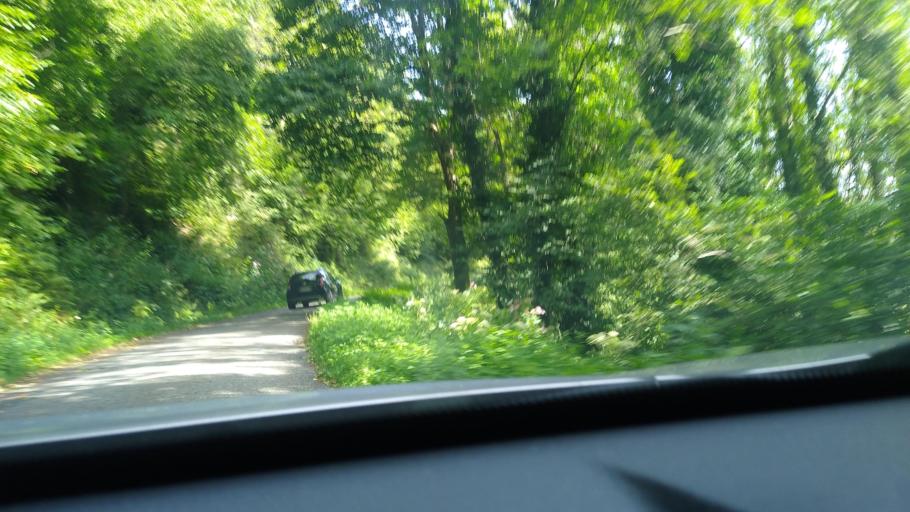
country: FR
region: Midi-Pyrenees
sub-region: Departement de l'Ariege
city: Saint-Girons
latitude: 42.7961
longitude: 1.1872
